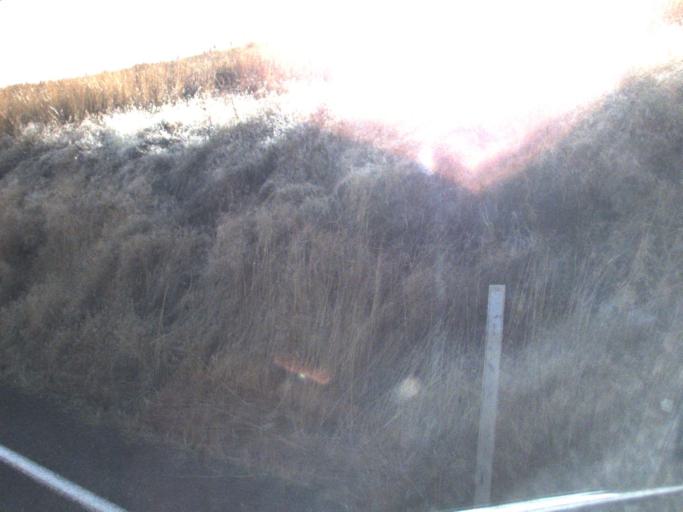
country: US
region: Washington
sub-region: Columbia County
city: Dayton
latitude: 46.4827
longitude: -117.9611
